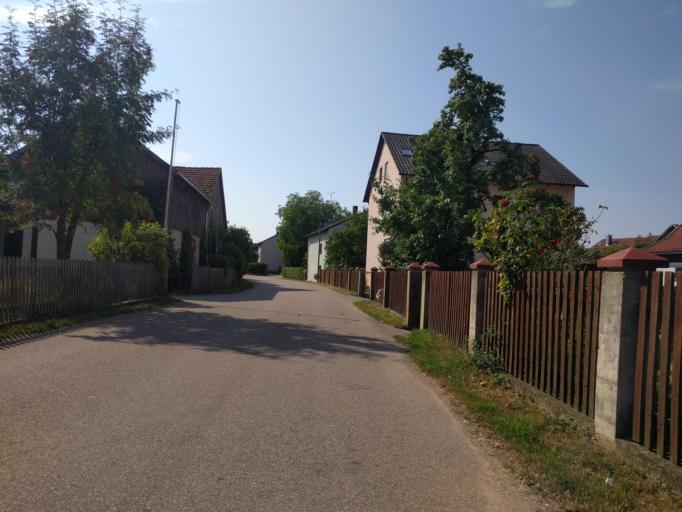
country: DE
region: Bavaria
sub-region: Upper Palatinate
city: Donaustauf
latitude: 49.0162
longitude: 12.2331
